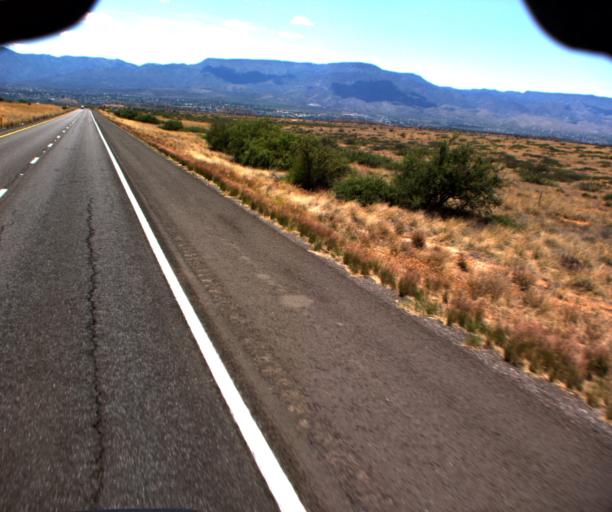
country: US
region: Arizona
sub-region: Yavapai County
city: Cornville
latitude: 34.7556
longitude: -111.9549
